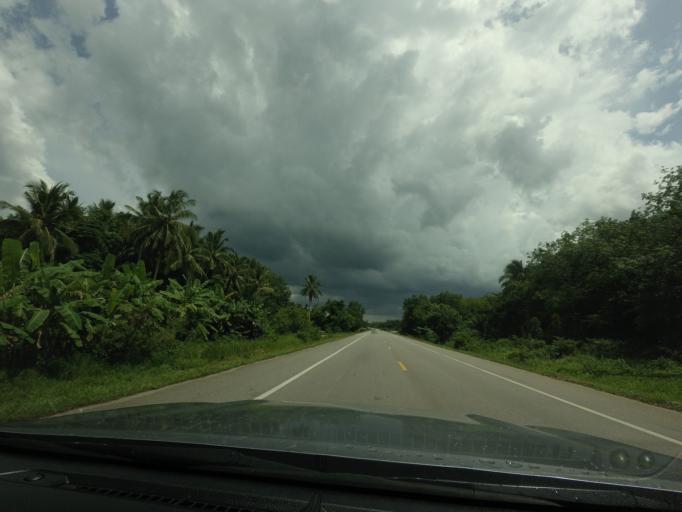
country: TH
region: Chumphon
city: Chumphon
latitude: 10.5681
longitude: 99.1659
